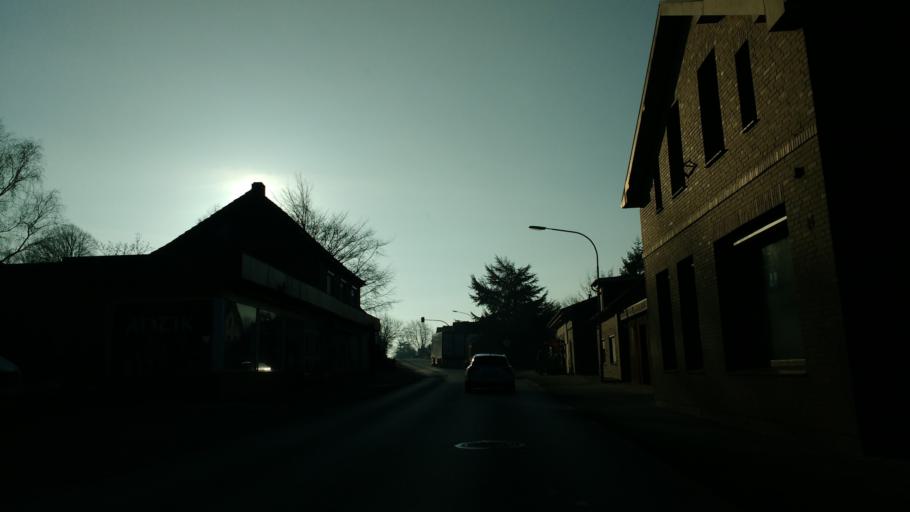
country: DE
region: Schleswig-Holstein
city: Schenefeld
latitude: 54.0445
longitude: 9.4808
